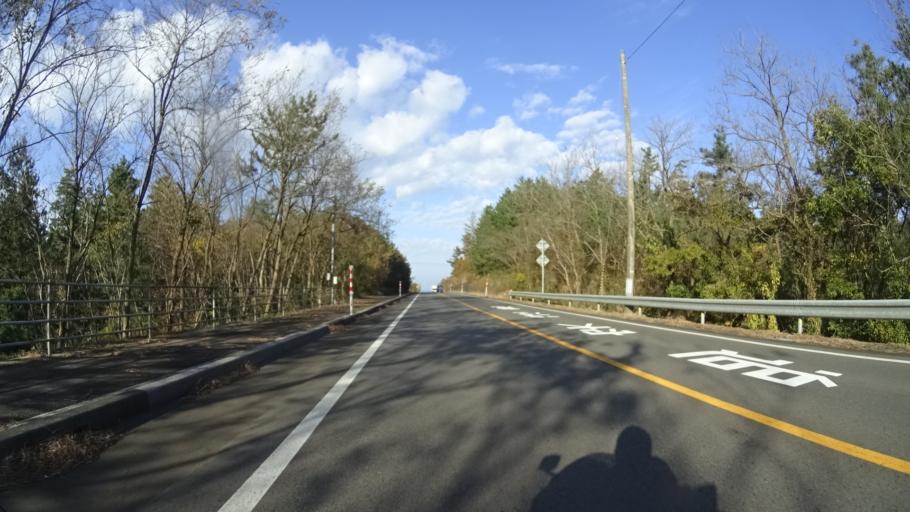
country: JP
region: Niigata
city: Kashiwazaki
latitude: 37.2853
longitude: 138.3993
